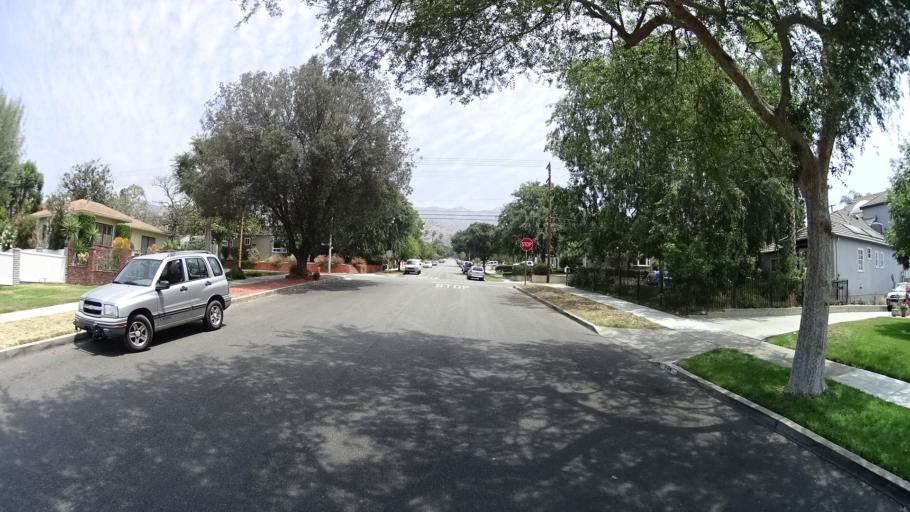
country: US
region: California
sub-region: Los Angeles County
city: Burbank
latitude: 34.1932
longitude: -118.3095
